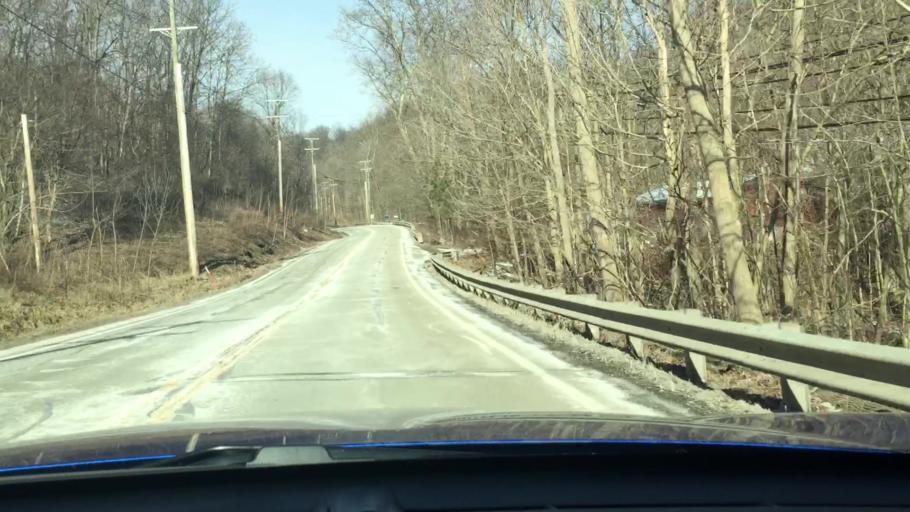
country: US
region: Pennsylvania
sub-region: Washington County
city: Canonsburg
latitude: 40.2847
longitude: -80.1552
